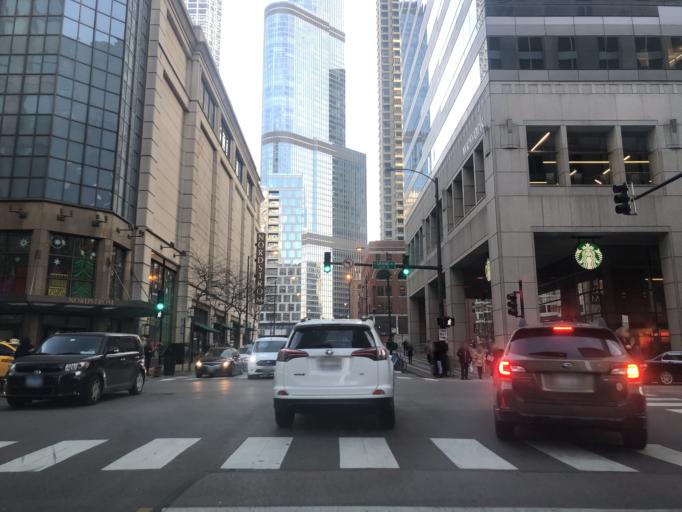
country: US
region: Illinois
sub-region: Cook County
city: Chicago
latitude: 41.8919
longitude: -87.6267
